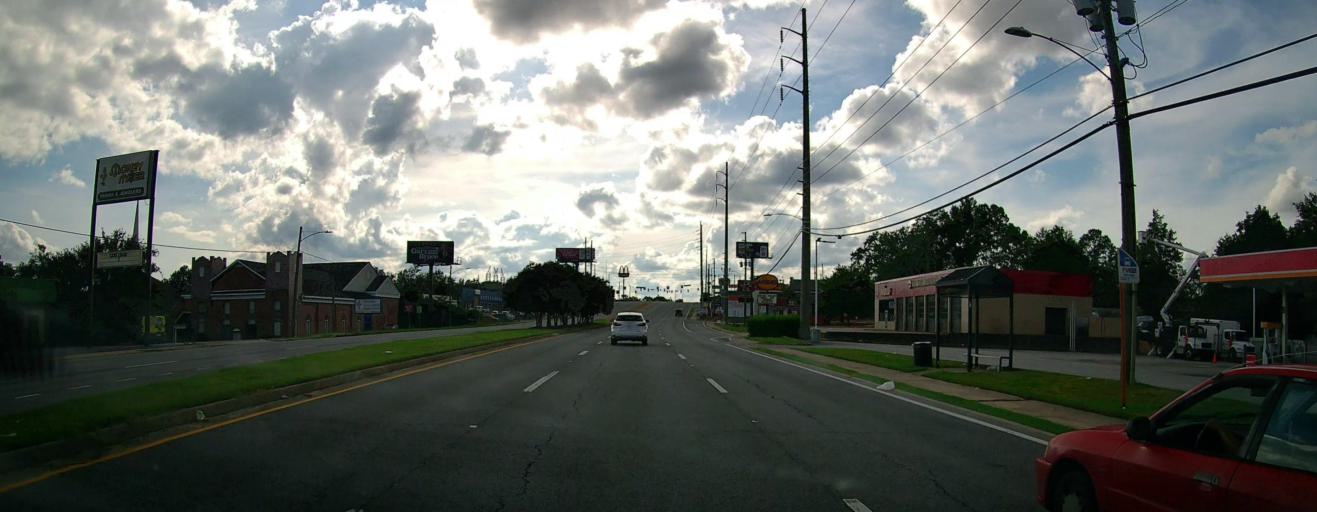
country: US
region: Alabama
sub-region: Russell County
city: Phenix City
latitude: 32.5071
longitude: -84.9669
